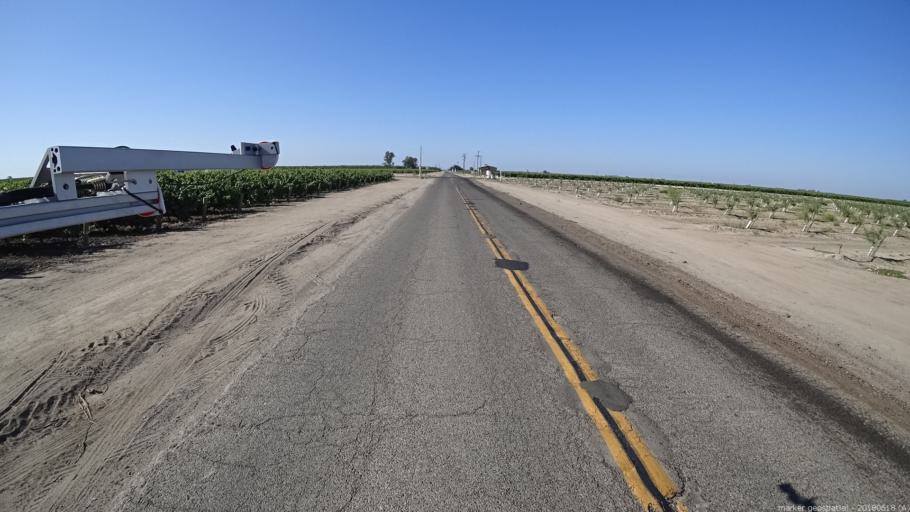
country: US
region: California
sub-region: Madera County
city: Parkwood
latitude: 36.8520
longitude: -120.1284
